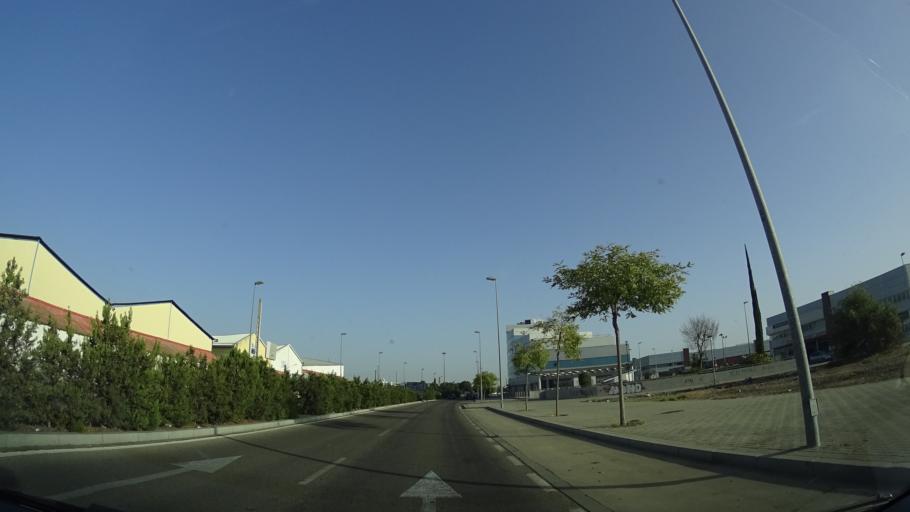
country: ES
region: Andalusia
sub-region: Provincia de Sevilla
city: Sevilla
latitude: 37.4252
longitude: -5.9783
